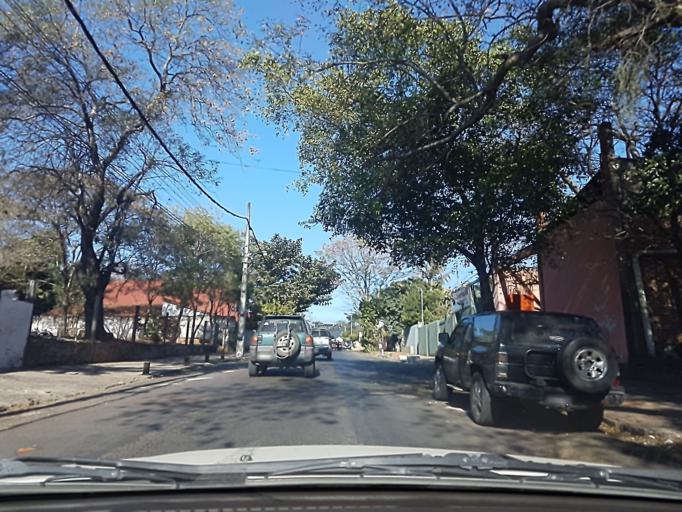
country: PY
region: Central
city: Lambare
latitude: -25.3129
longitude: -57.5857
